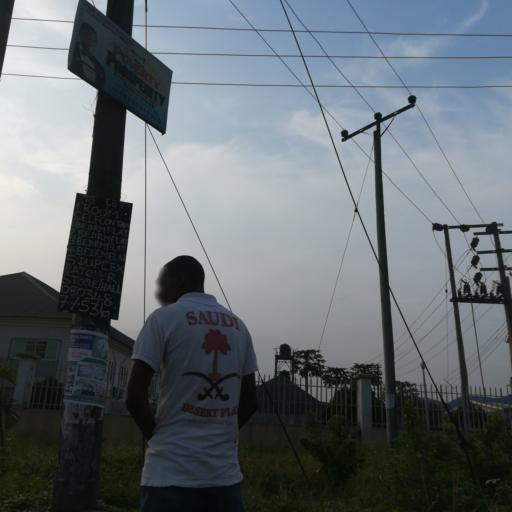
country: NG
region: Rivers
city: Port Harcourt
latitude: 4.8449
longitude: 7.0418
